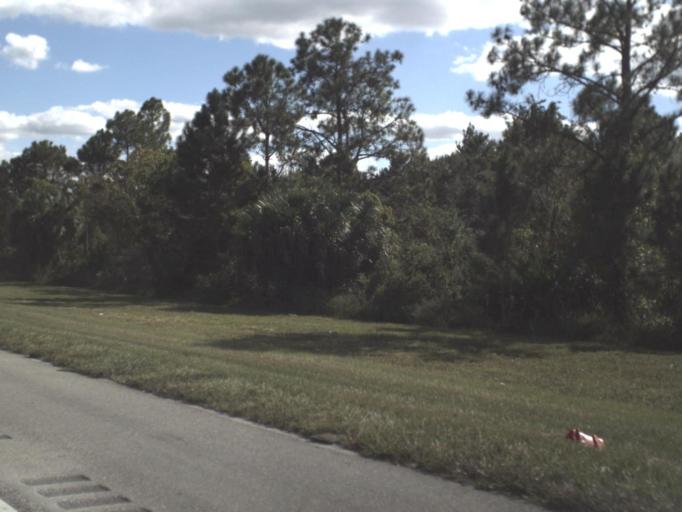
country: US
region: Florida
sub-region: Indian River County
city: Fellsmere
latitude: 27.5976
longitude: -80.8205
